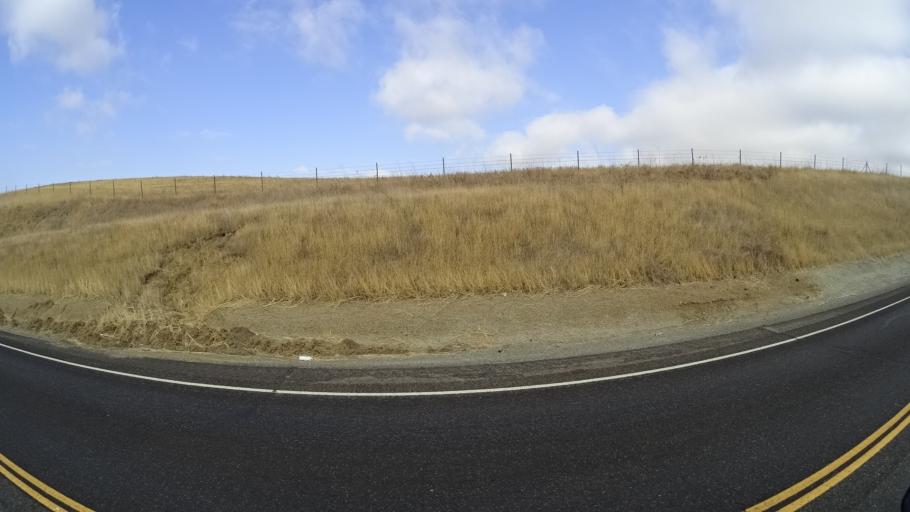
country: US
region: California
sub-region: Yolo County
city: Dunnigan
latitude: 38.7784
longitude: -121.9386
